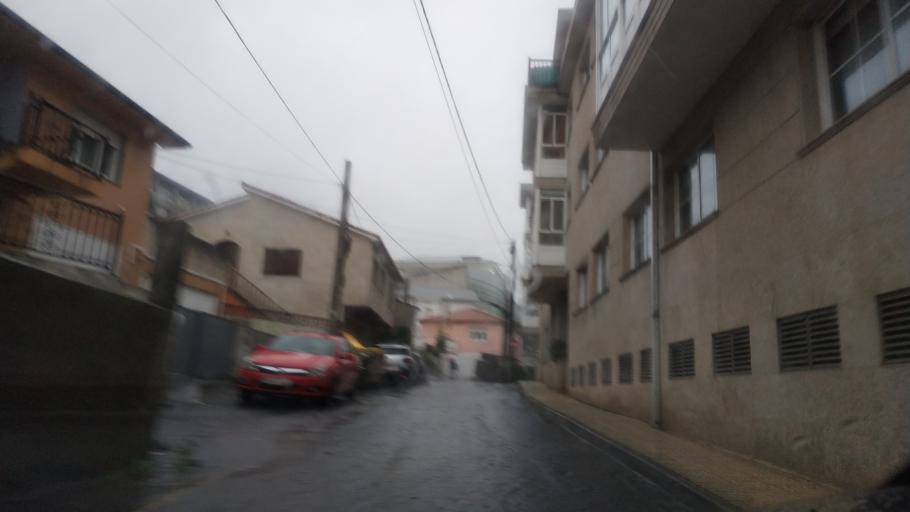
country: ES
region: Galicia
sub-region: Provincia da Coruna
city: A Coruna
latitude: 43.3295
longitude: -8.4085
